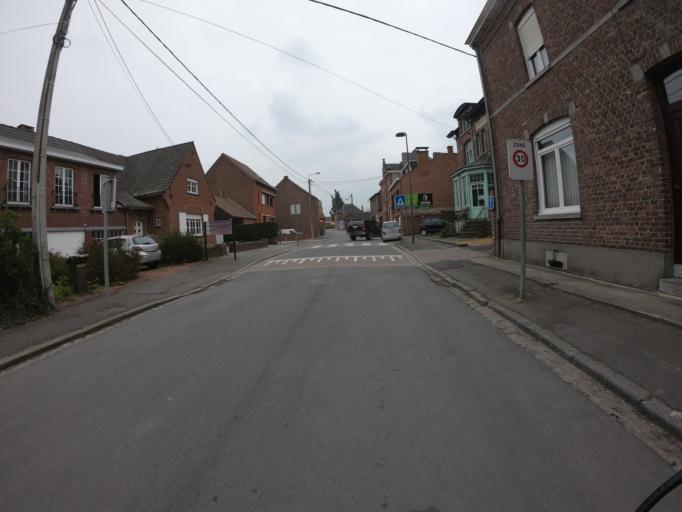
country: BE
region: Wallonia
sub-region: Province du Hainaut
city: Flobecq
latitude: 50.7385
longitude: 3.7441
